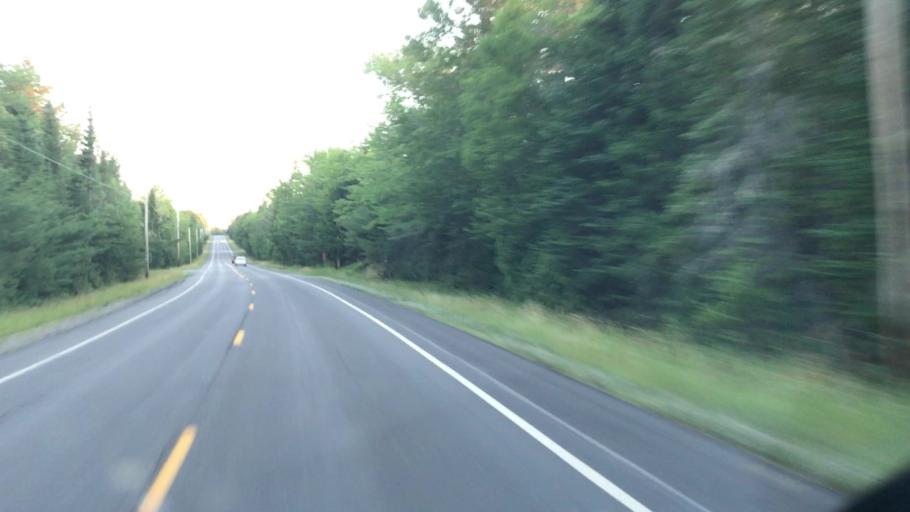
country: US
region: Maine
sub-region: Penobscot County
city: Medway
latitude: 45.5772
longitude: -68.3194
